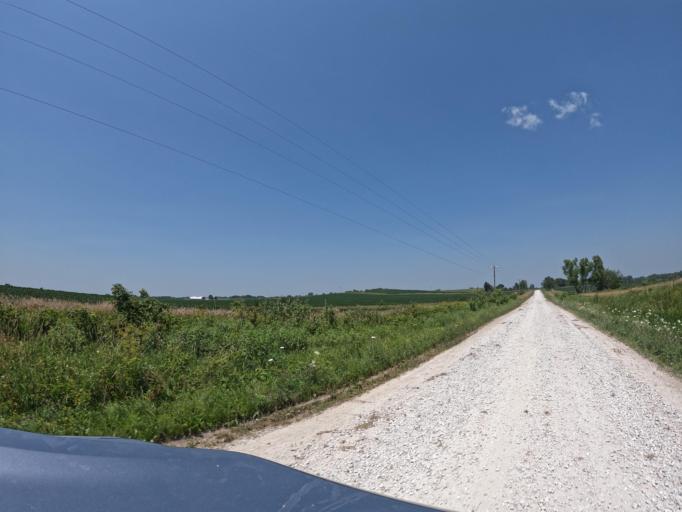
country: US
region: Iowa
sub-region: Keokuk County
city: Sigourney
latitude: 41.2908
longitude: -92.2095
